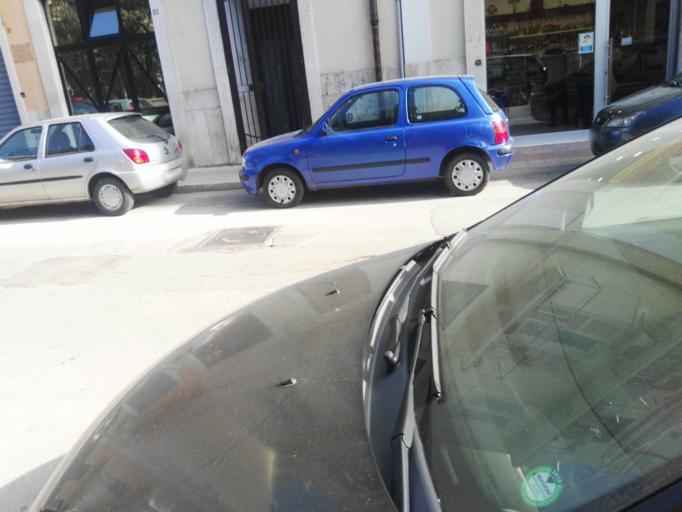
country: IT
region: Apulia
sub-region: Provincia di Bari
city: Bitonto
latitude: 41.1132
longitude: 16.6973
